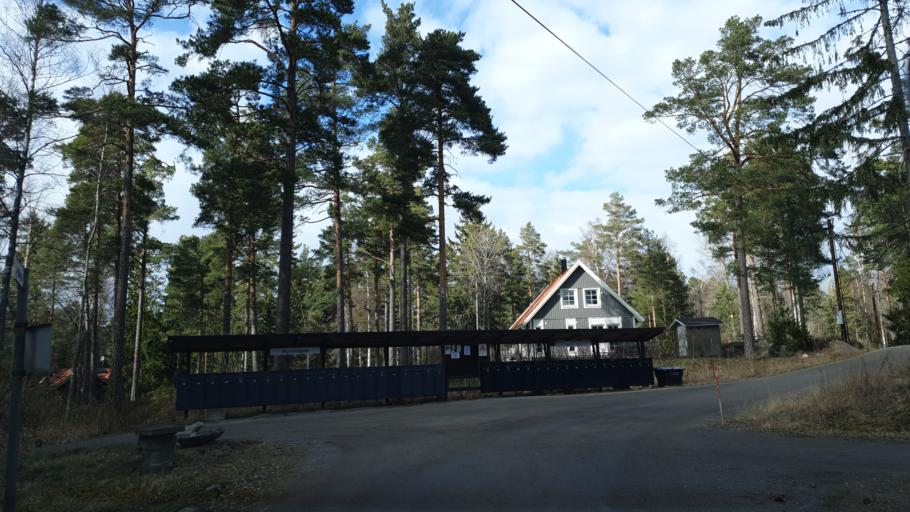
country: SE
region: Stockholm
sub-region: Varmdo Kommun
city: Mortnas
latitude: 59.2627
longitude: 18.4269
